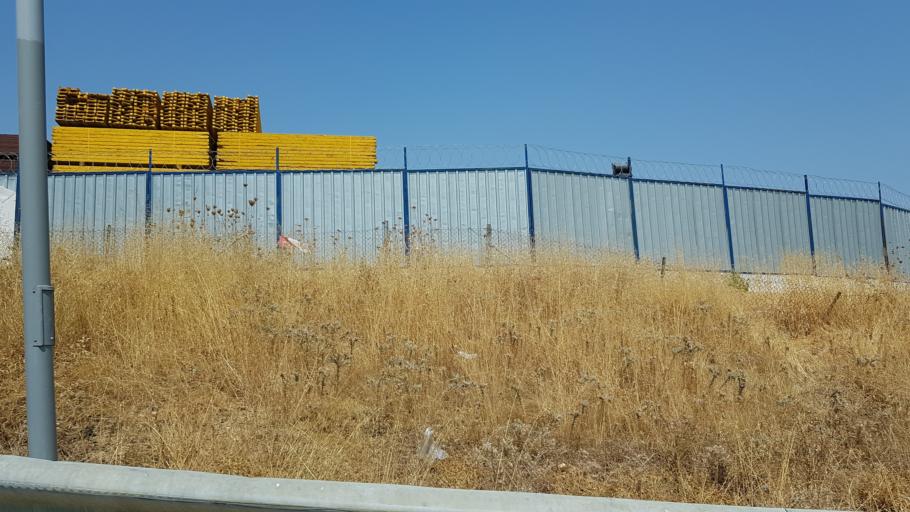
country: TR
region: Izmir
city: Karabaglar
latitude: 38.3591
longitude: 27.1042
